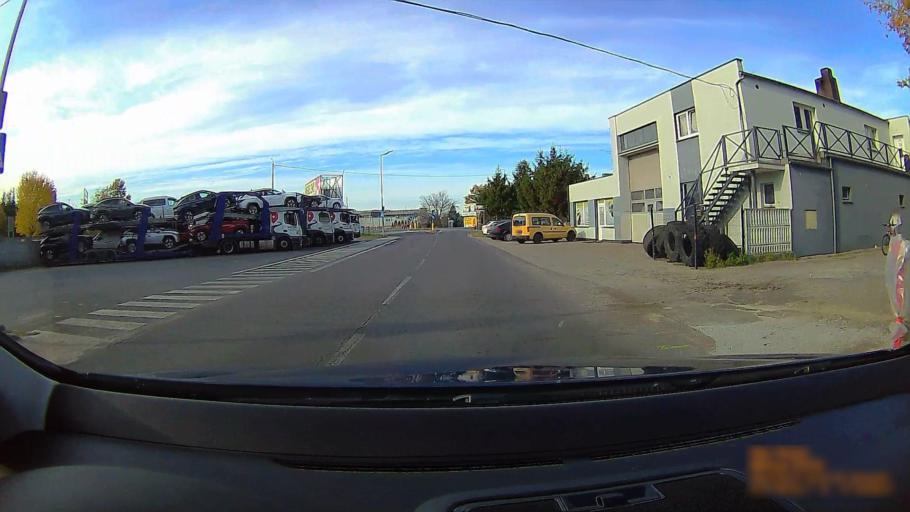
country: PL
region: Greater Poland Voivodeship
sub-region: Powiat ostrzeszowski
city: Ostrzeszow
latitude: 51.4361
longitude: 17.9166
